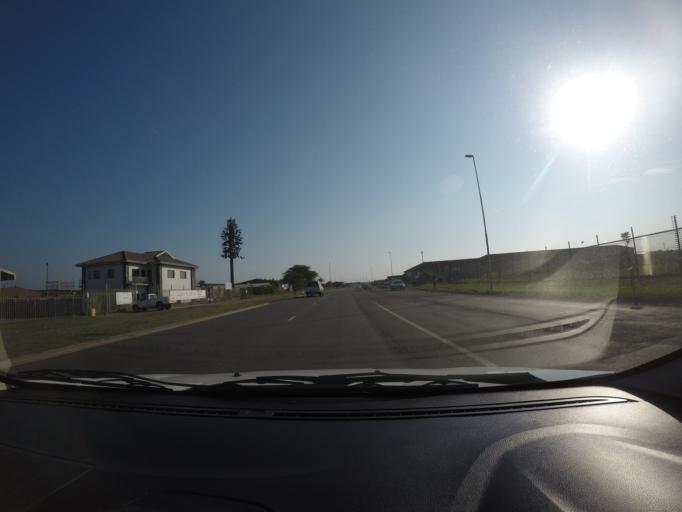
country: ZA
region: KwaZulu-Natal
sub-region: uThungulu District Municipality
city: Richards Bay
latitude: -28.7471
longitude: 32.0327
